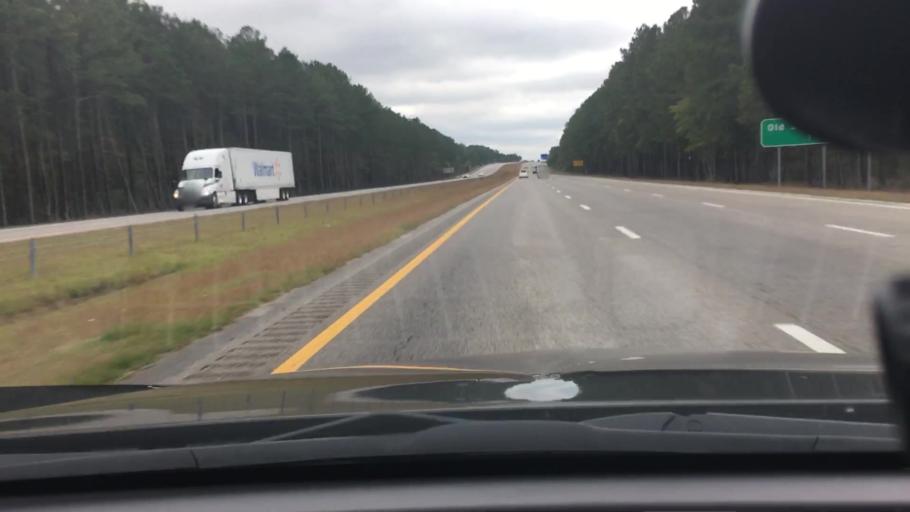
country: US
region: North Carolina
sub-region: Wilson County
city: Wilson
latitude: 35.6724
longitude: -77.8637
